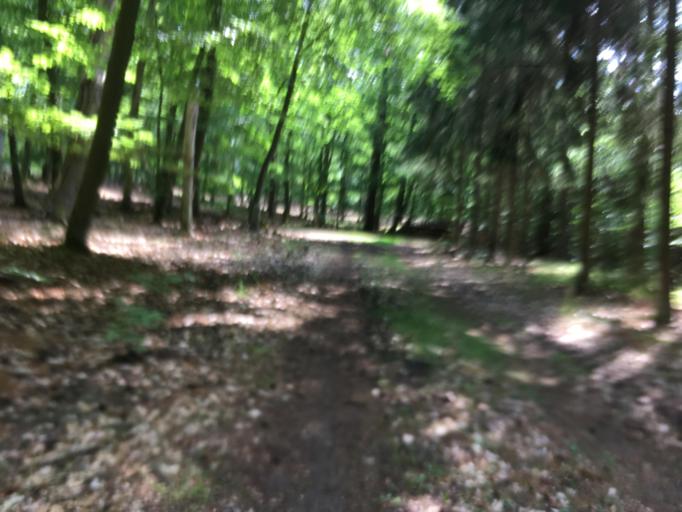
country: DE
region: Brandenburg
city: Joachimsthal
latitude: 53.0024
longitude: 13.7741
